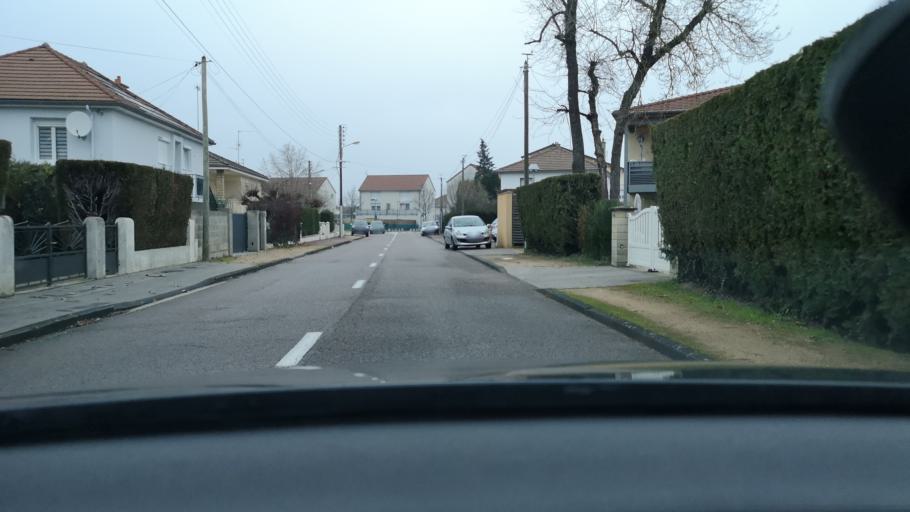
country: FR
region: Bourgogne
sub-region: Departement de Saone-et-Loire
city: Chalon-sur-Saone
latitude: 46.8043
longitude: 4.8500
